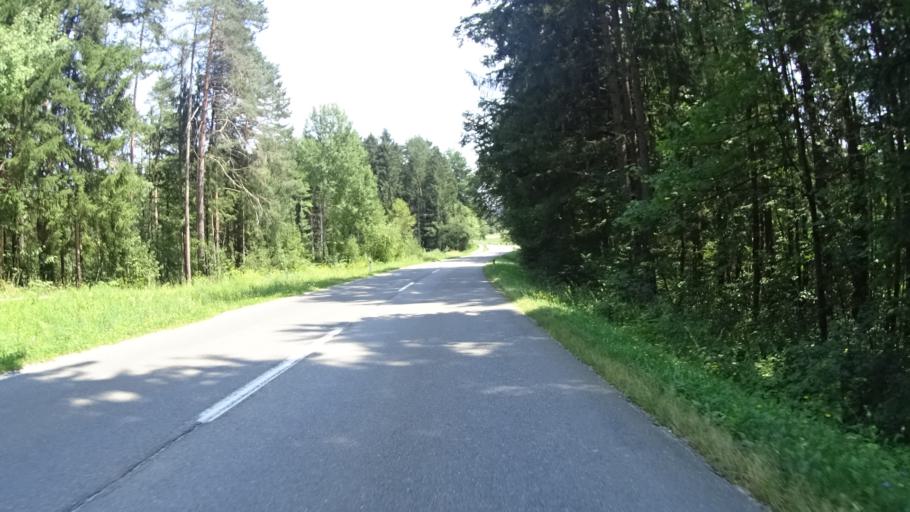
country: SI
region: Mezica
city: Mezica
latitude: 46.5576
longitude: 14.8528
